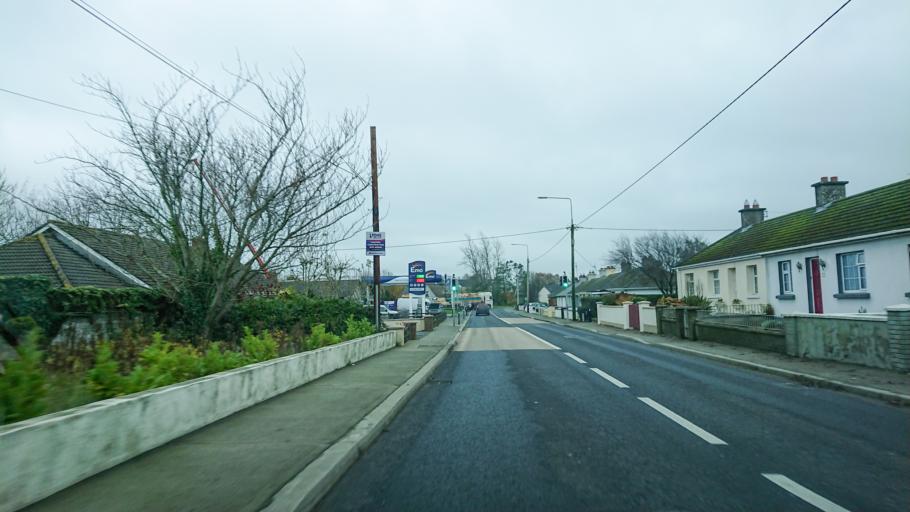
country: IE
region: Leinster
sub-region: Kilkenny
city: Mooncoin
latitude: 52.2920
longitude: -7.2535
